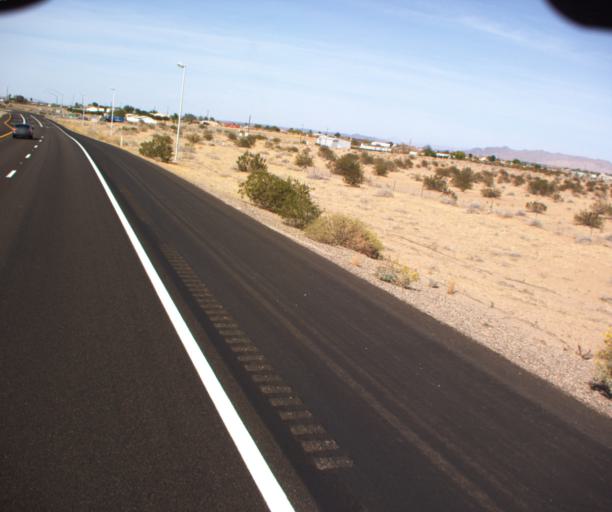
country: US
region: Arizona
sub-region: Yuma County
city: Fortuna Foothills
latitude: 32.6240
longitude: -114.5200
